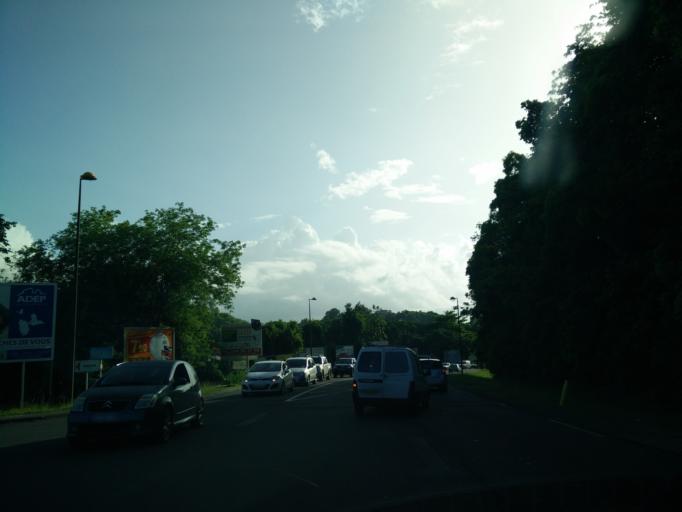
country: GP
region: Guadeloupe
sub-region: Guadeloupe
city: Les Abymes
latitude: 16.2520
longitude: -61.5151
